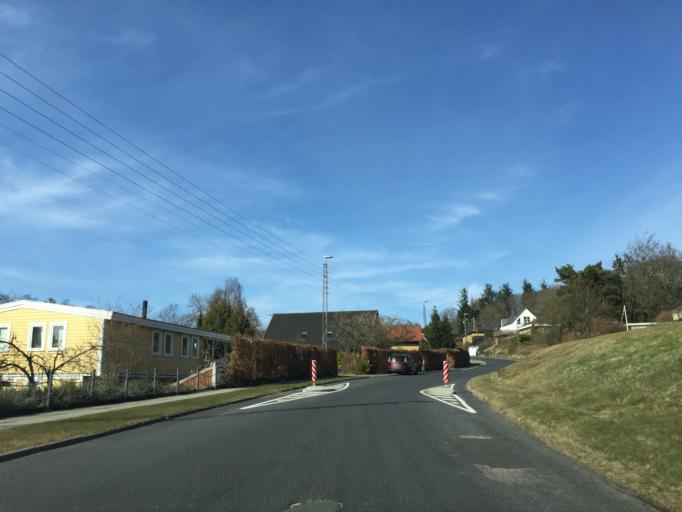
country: DK
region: Central Jutland
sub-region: Silkeborg Kommune
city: Silkeborg
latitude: 56.1881
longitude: 9.5421
